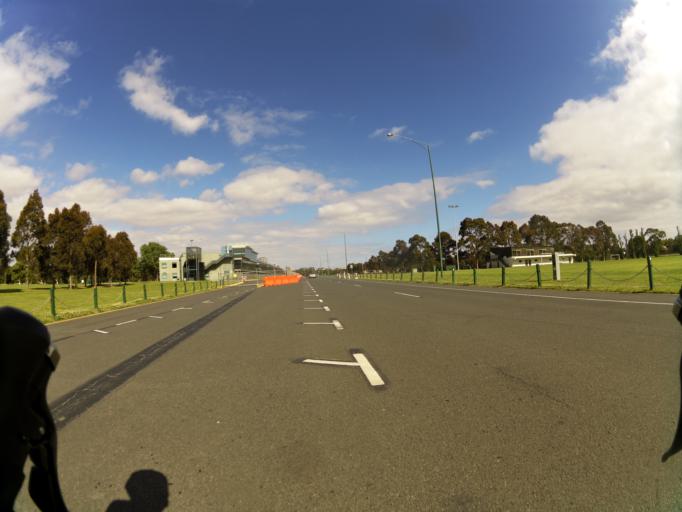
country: AU
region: Victoria
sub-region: Port Phillip
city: Middle Park
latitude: -37.8491
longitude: 144.9679
